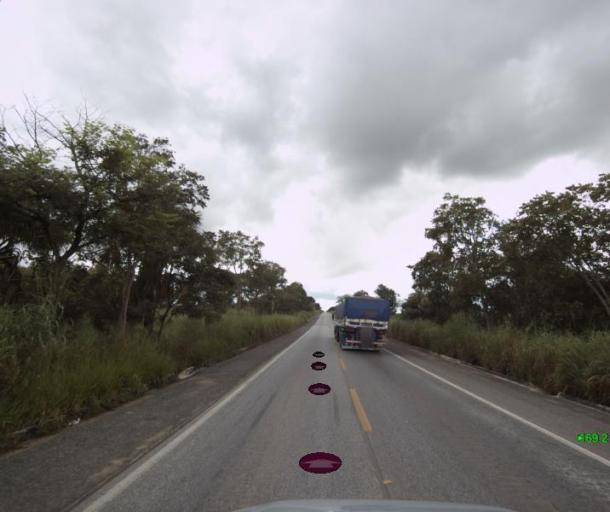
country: BR
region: Goias
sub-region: Uruacu
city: Uruacu
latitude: -14.2541
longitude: -49.1406
